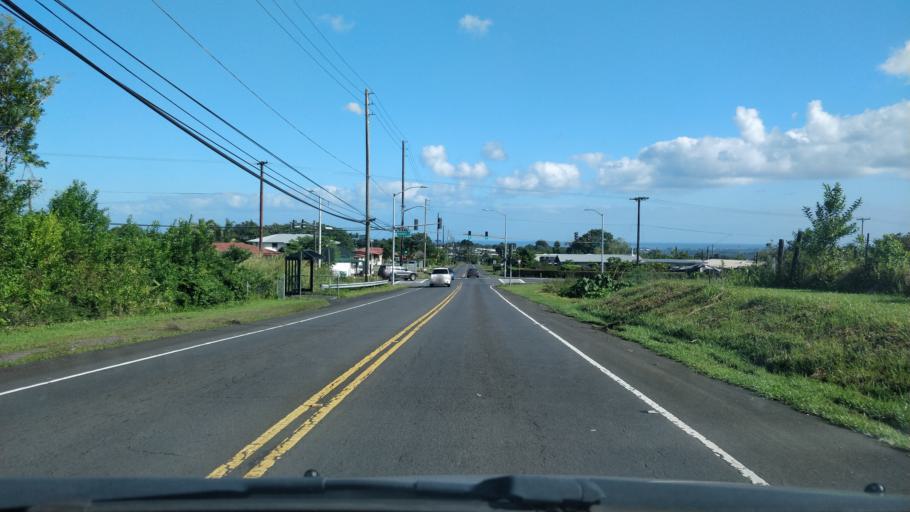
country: US
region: Hawaii
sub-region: Hawaii County
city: Hilo
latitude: 19.6721
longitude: -155.0930
